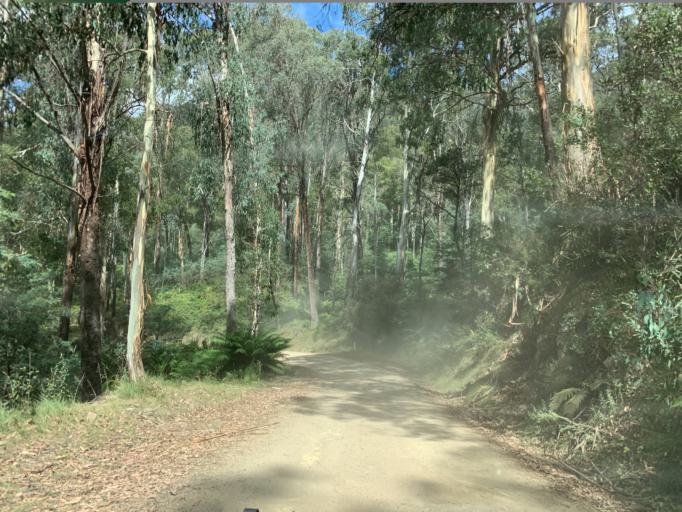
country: AU
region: Victoria
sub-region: Mansfield
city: Mansfield
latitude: -37.1042
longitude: 146.4999
